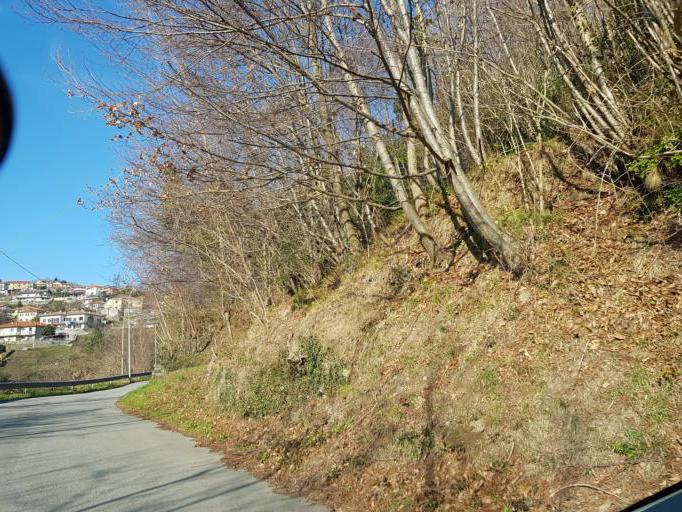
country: IT
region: Liguria
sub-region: Provincia di Genova
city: Campomorone
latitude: 44.5014
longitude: 8.8759
